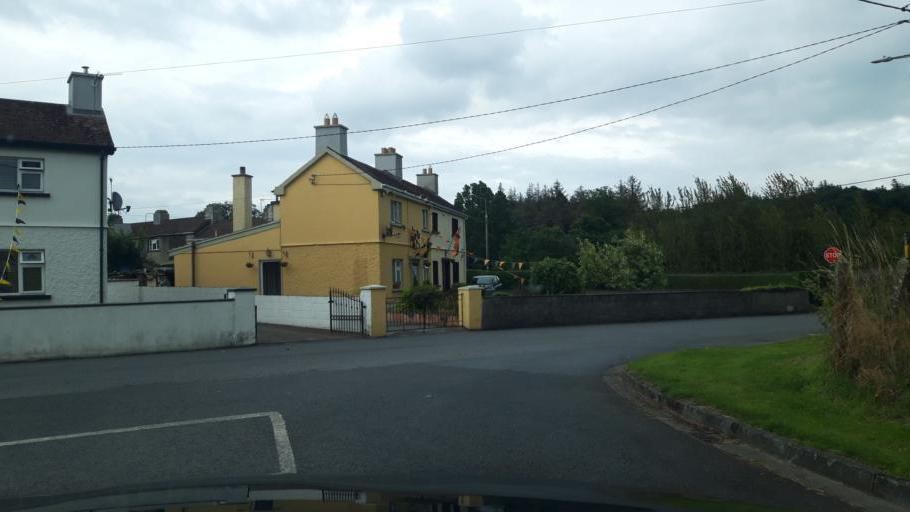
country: IE
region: Leinster
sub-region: Kilkenny
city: Castlecomer
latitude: 52.8003
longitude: -7.2108
